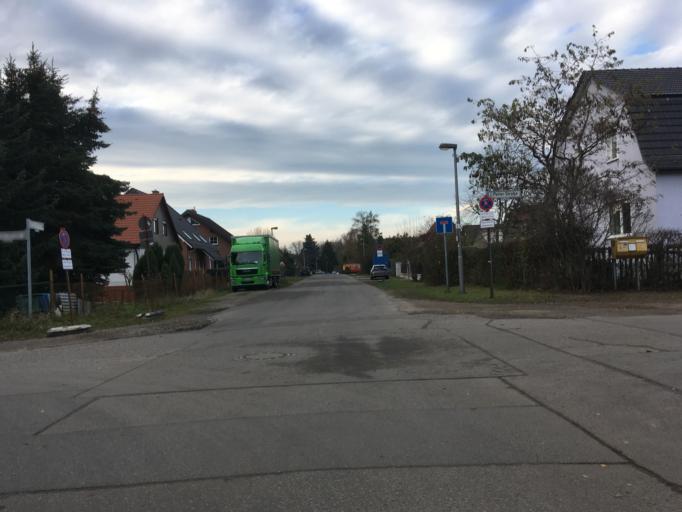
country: DE
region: Berlin
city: Weissensee
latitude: 52.5635
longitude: 13.4860
